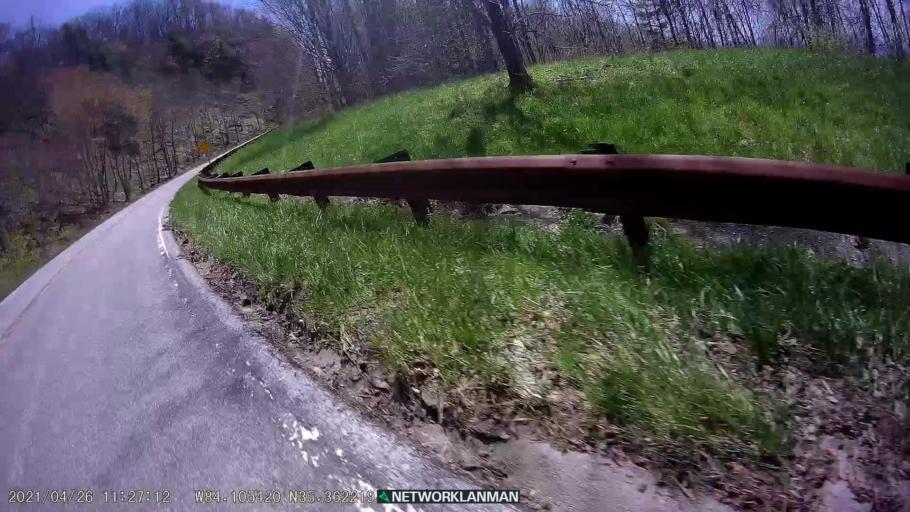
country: US
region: Tennessee
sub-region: Monroe County
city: Vonore
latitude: 35.3622
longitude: -84.1055
